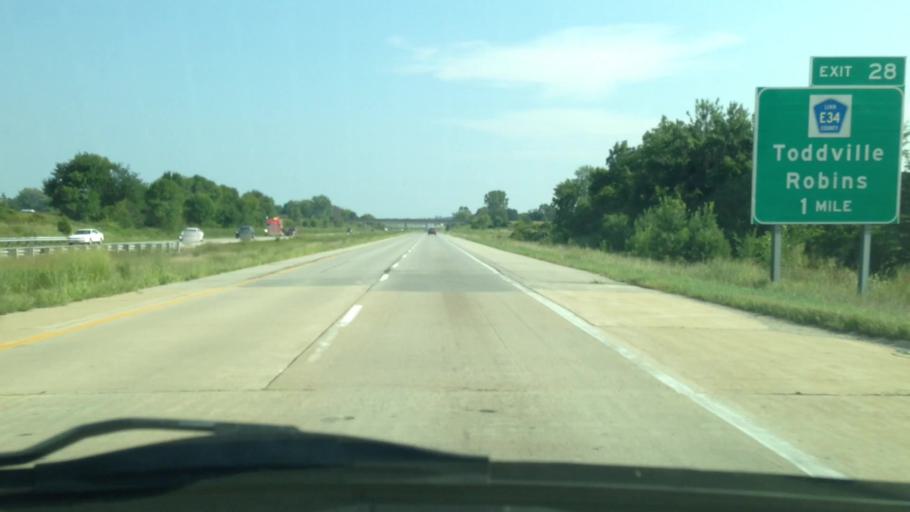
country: US
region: Iowa
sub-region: Linn County
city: Robins
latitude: 42.1109
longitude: -91.7083
